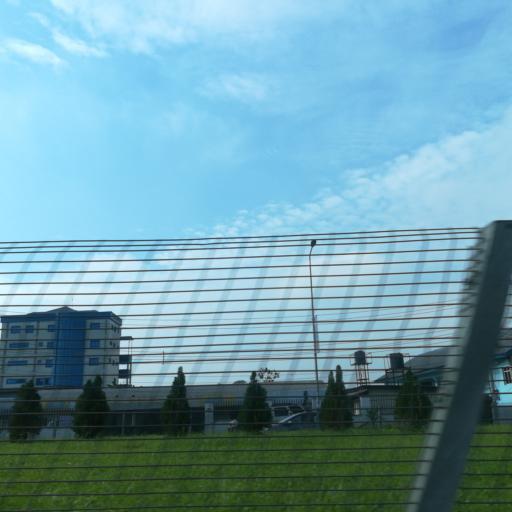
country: NG
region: Rivers
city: Port Harcourt
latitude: 4.8096
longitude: 7.0184
